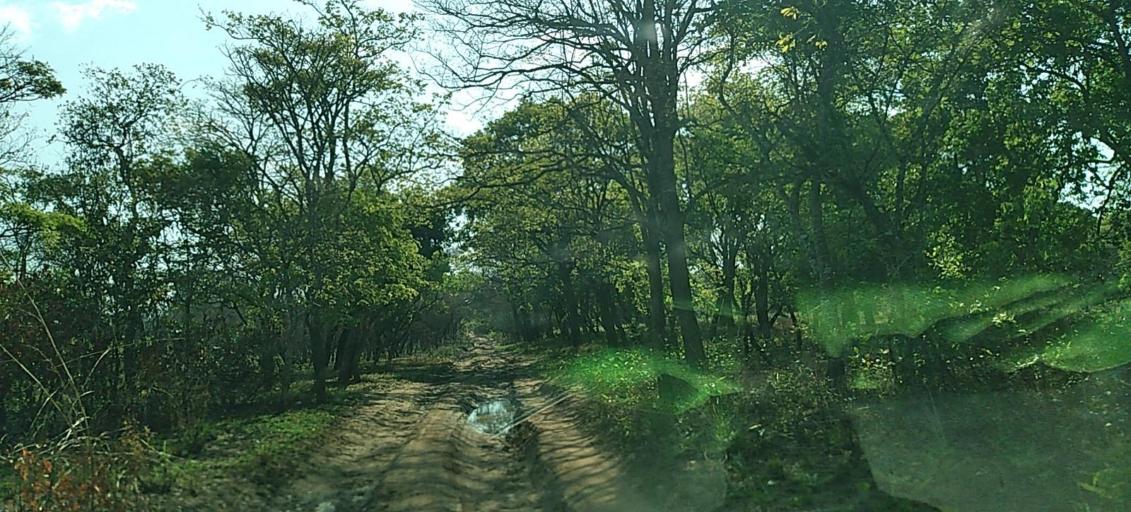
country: ZM
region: North-Western
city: Mwinilunga
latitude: -11.3008
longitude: 24.8471
